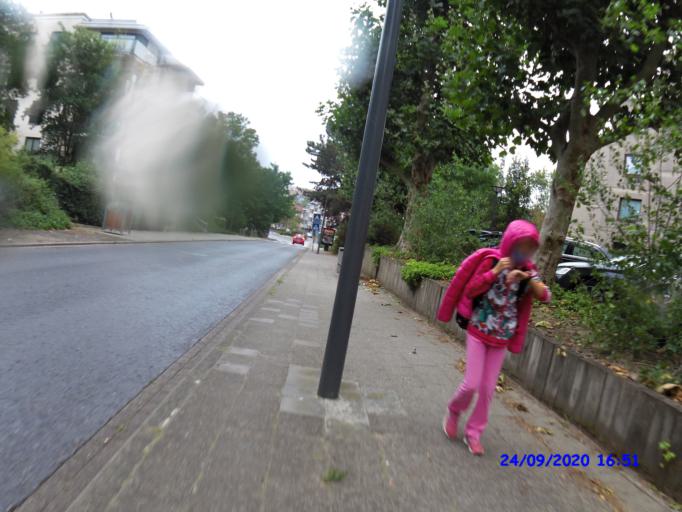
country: BE
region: Flanders
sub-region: Provincie Vlaams-Brabant
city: Kraainem
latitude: 50.8511
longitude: 4.4276
